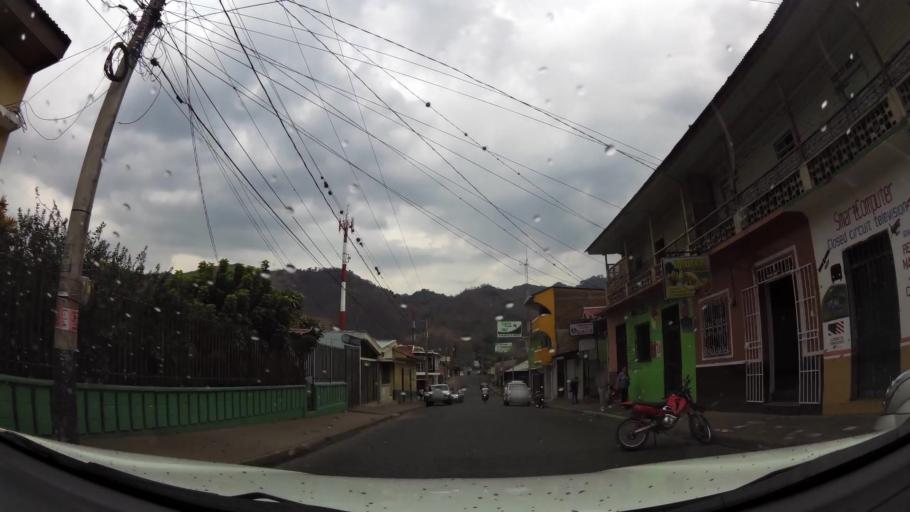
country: NI
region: Jinotega
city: Jinotega
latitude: 13.0914
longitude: -86.0015
